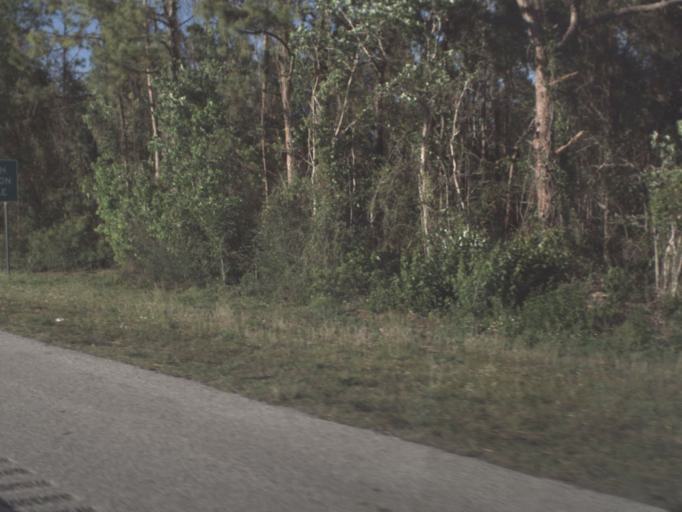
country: US
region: Florida
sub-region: Flagler County
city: Flagler Beach
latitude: 29.4884
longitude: -81.1884
